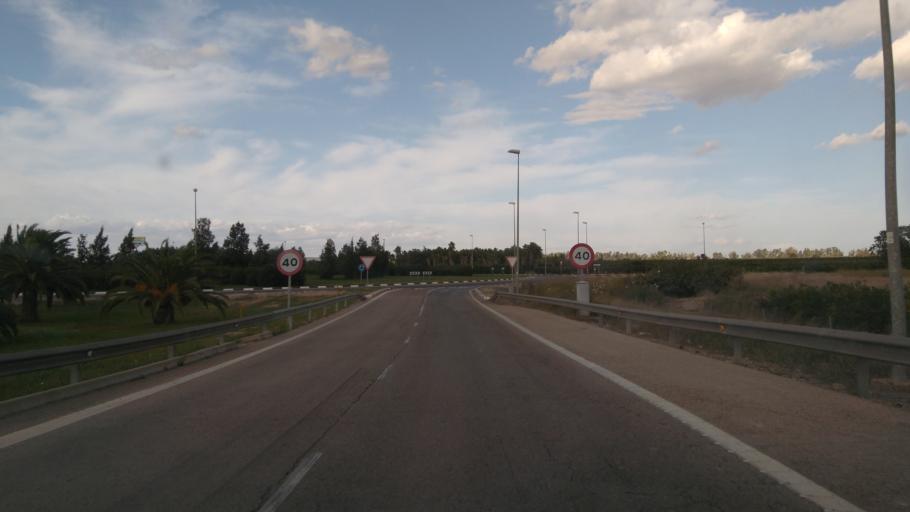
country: ES
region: Valencia
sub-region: Provincia de Valencia
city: L'Alcudia
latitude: 39.1917
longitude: -0.4932
